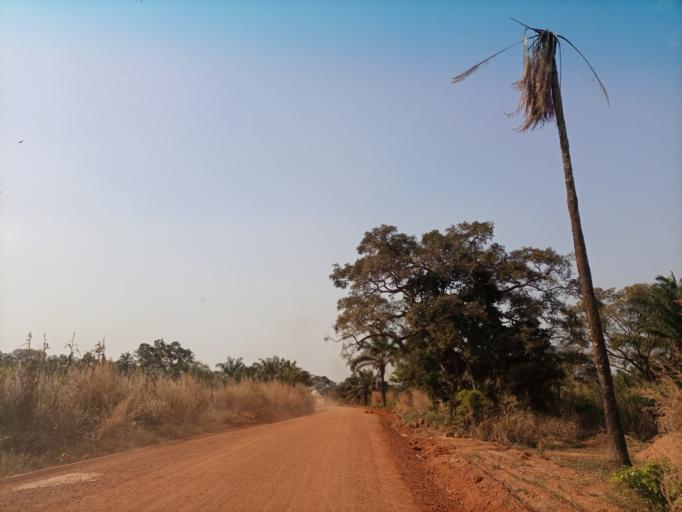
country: NG
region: Enugu
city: Aku
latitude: 6.7032
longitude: 7.3153
